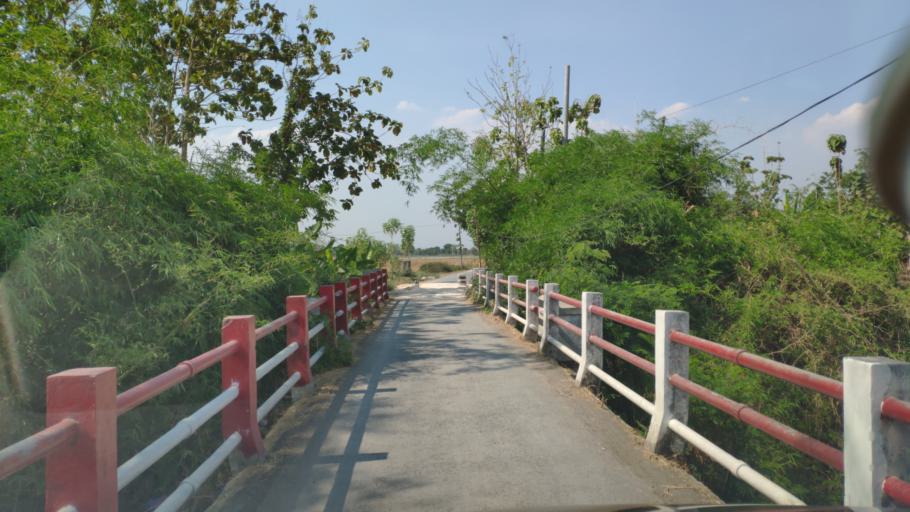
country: ID
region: Central Java
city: Panolan
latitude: -7.2203
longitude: 111.5333
